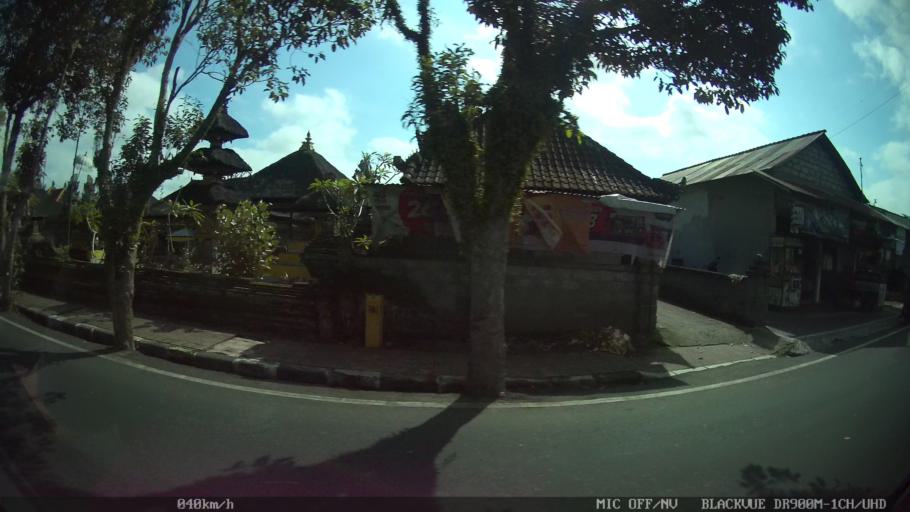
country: ID
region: Bali
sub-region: Kabupaten Gianyar
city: Ubud
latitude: -8.5112
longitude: 115.2931
